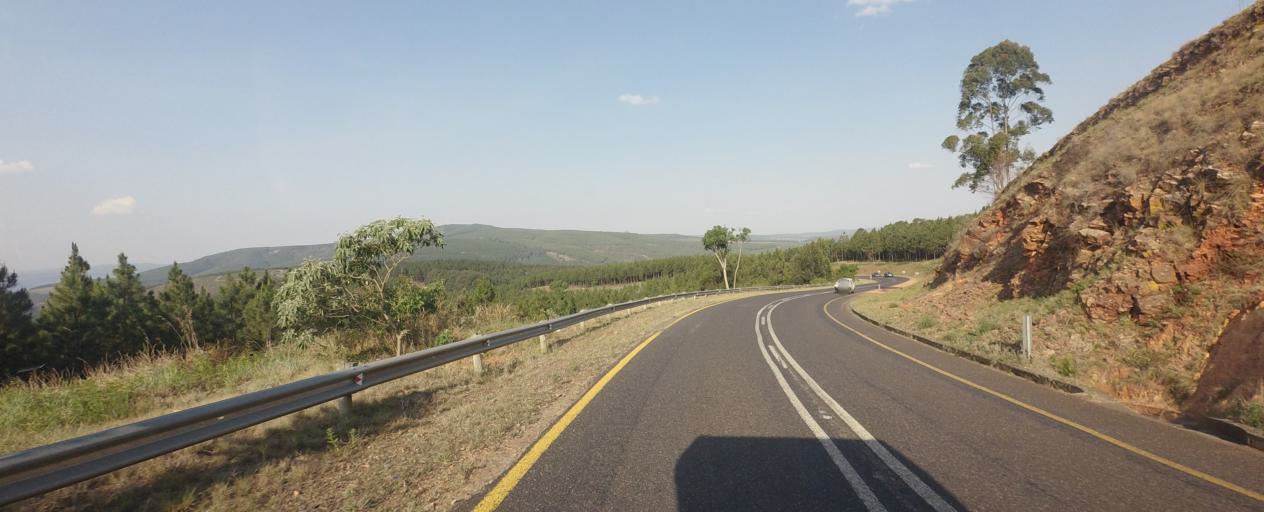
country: ZA
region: Mpumalanga
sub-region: Ehlanzeni District
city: Lydenburg
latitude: -25.1783
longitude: 30.7090
